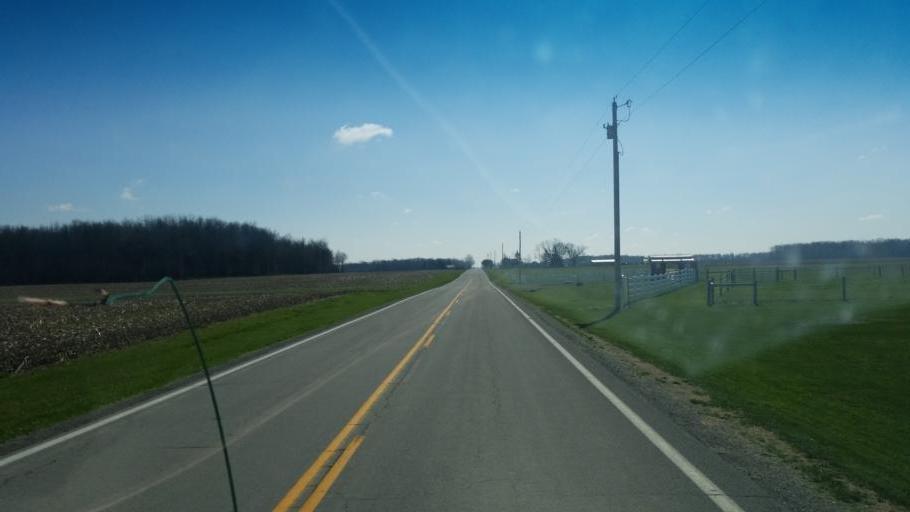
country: US
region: Ohio
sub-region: Wyandot County
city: Upper Sandusky
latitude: 40.7376
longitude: -83.3510
